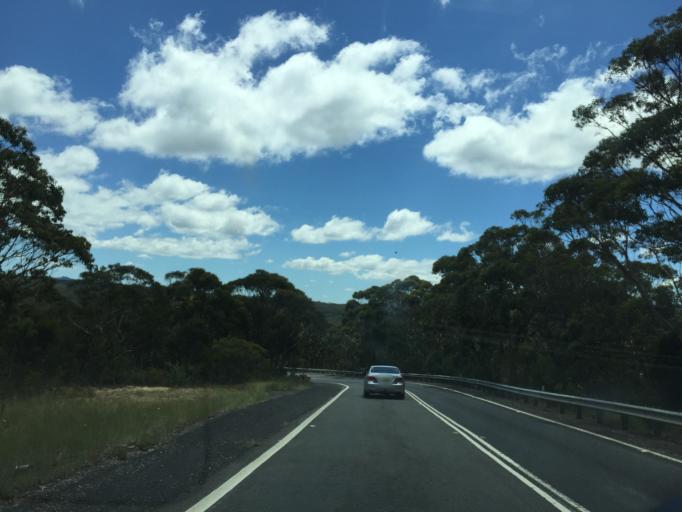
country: AU
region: New South Wales
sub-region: Blue Mountains Municipality
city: Blackheath
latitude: -33.5452
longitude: 150.3888
